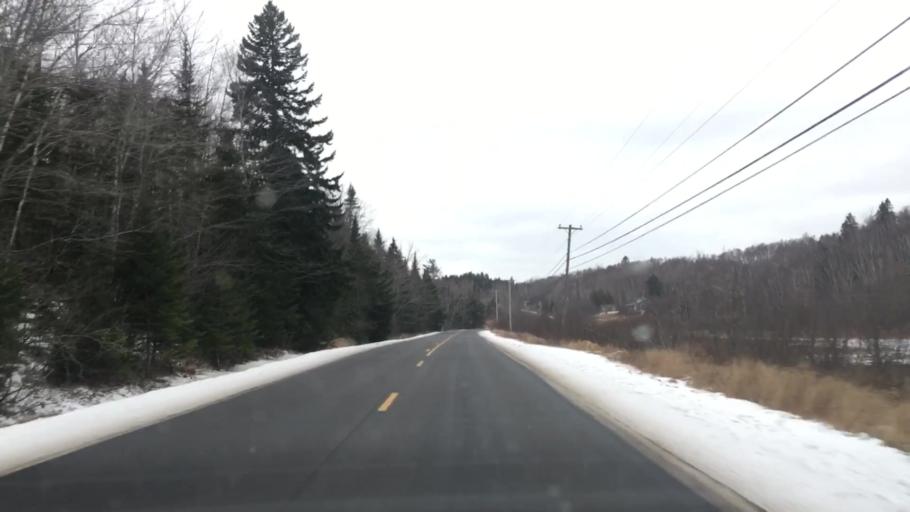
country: US
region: Maine
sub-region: Washington County
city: Machiasport
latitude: 44.7106
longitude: -67.3707
